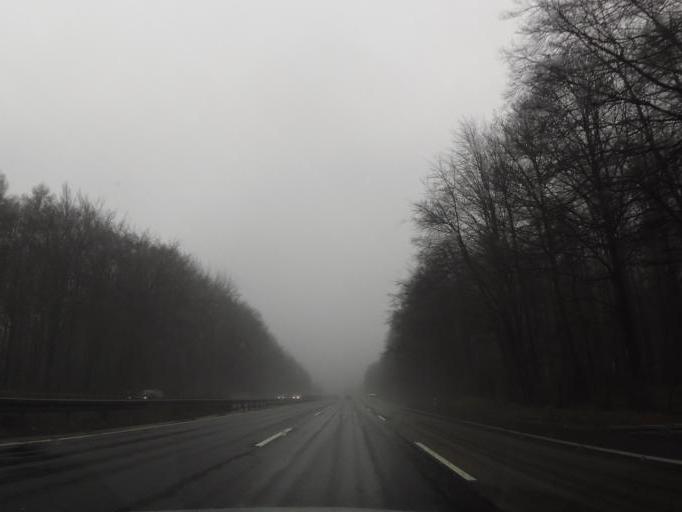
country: DE
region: Hesse
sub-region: Regierungsbezirk Darmstadt
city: Niedernhausen
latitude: 50.1372
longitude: 8.3331
